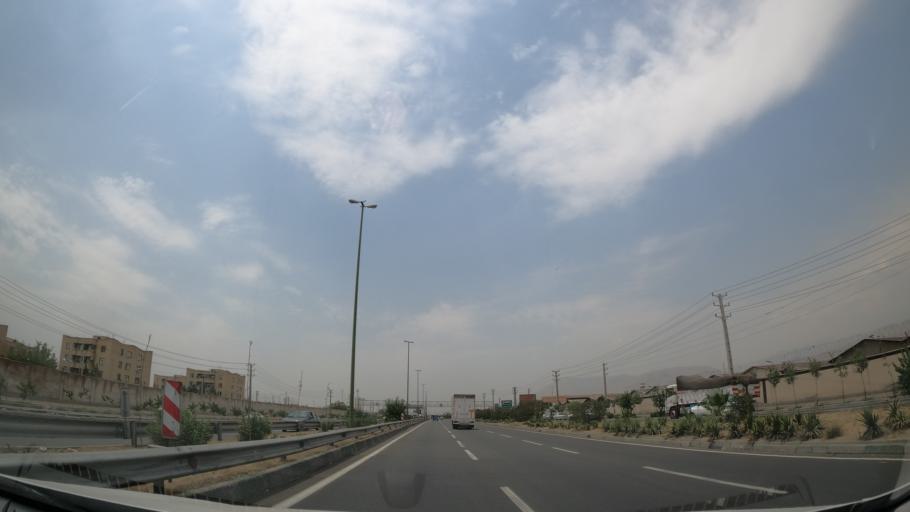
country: IR
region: Tehran
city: Shahr-e Qods
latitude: 35.6962
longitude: 51.2017
